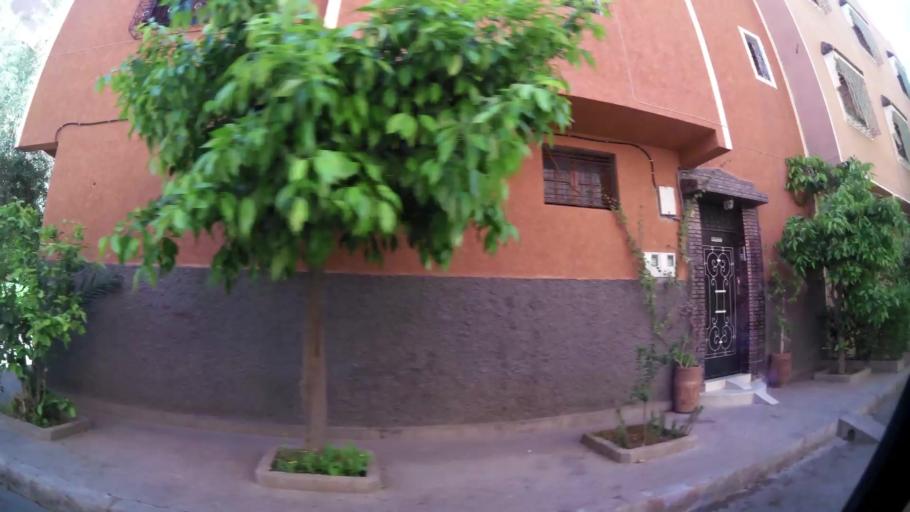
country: MA
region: Marrakech-Tensift-Al Haouz
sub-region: Marrakech
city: Marrakesh
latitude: 31.6610
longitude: -7.9880
